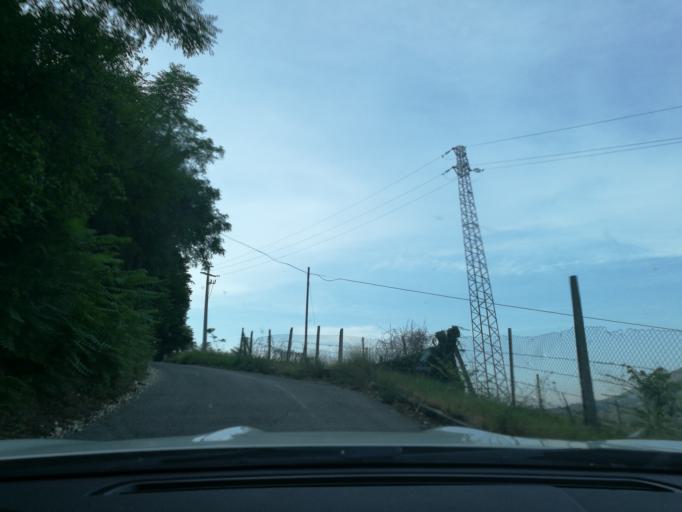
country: IT
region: Umbria
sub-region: Provincia di Terni
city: San Gemini
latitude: 42.6146
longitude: 12.5492
